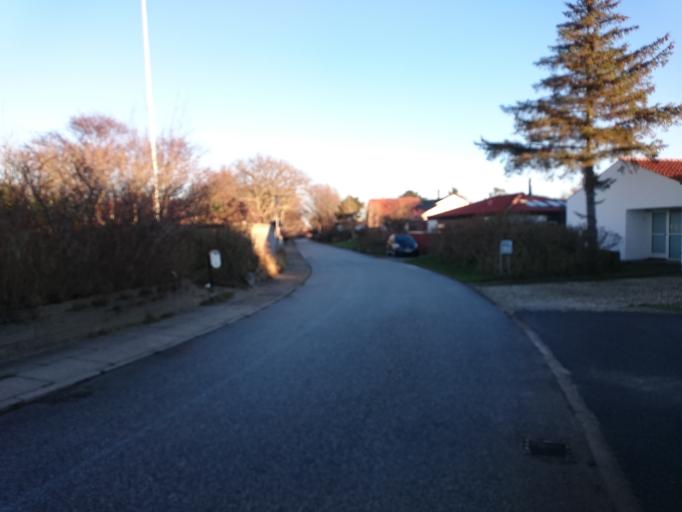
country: DK
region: North Denmark
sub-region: Frederikshavn Kommune
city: Skagen
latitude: 57.7161
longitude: 10.5671
